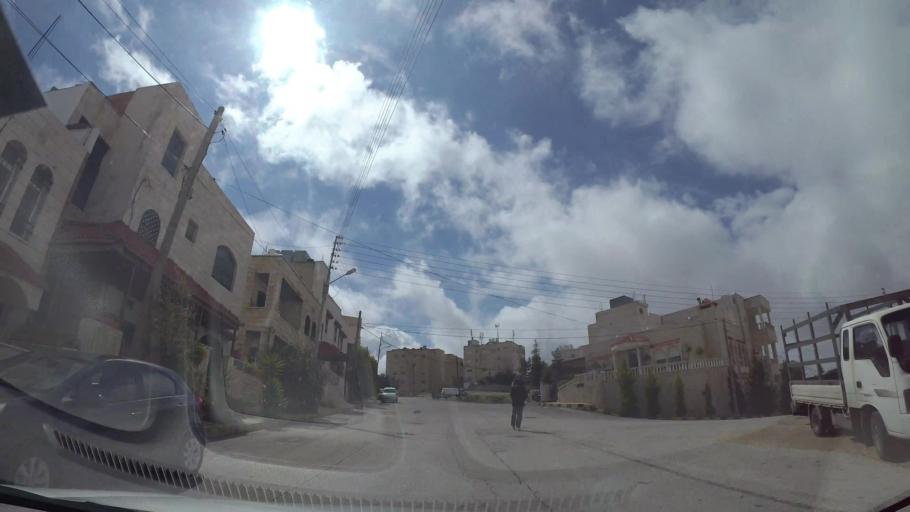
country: JO
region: Amman
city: Al Jubayhah
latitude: 32.0617
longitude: 35.8738
